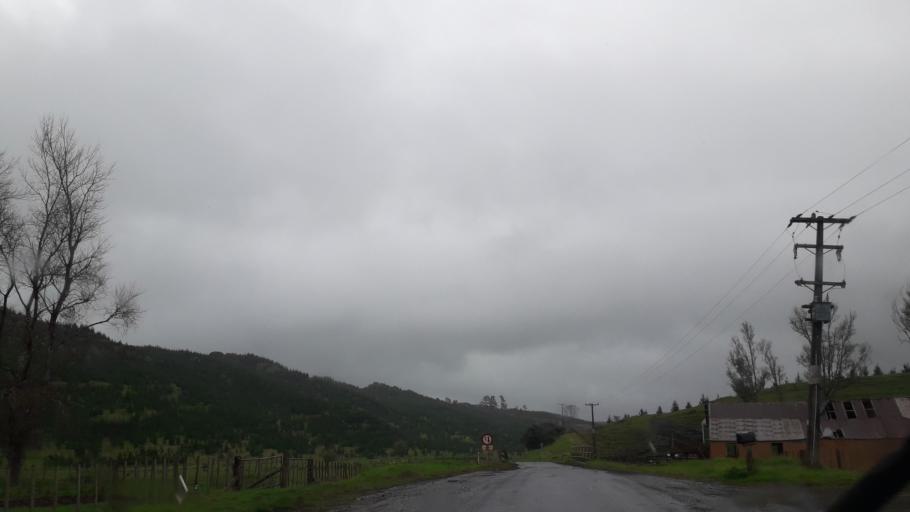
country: NZ
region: Northland
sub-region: Far North District
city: Ahipara
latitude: -35.4246
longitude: 173.3576
